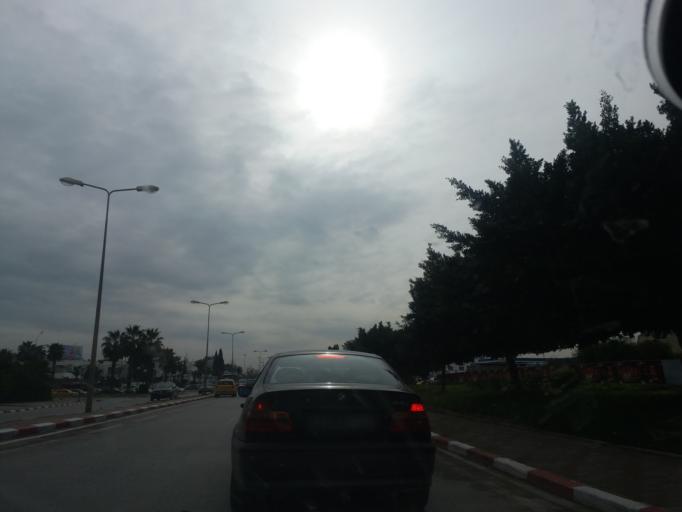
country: TN
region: Tunis
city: Tunis
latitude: 36.8440
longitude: 10.1643
